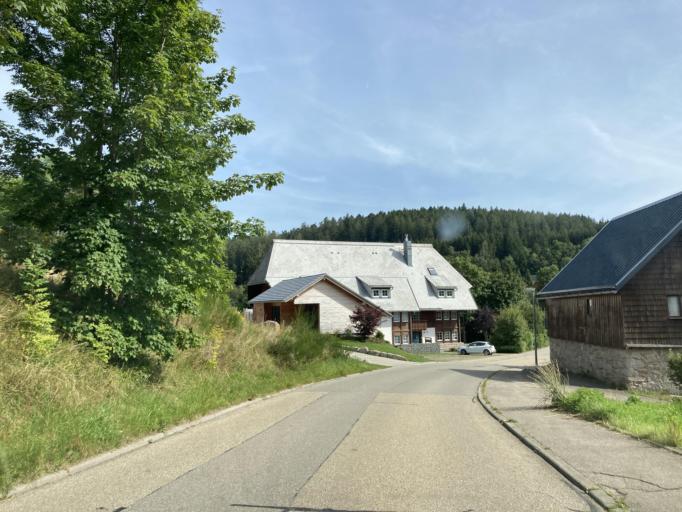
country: DE
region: Baden-Wuerttemberg
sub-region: Freiburg Region
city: Sankt Georgen im Schwarzwald
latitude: 48.1154
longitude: 8.3074
